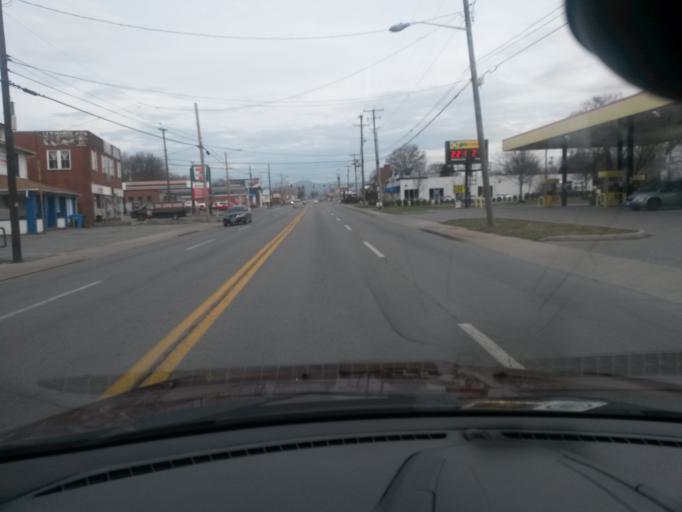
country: US
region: Virginia
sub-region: City of Roanoke
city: Roanoke
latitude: 37.3029
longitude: -79.9441
